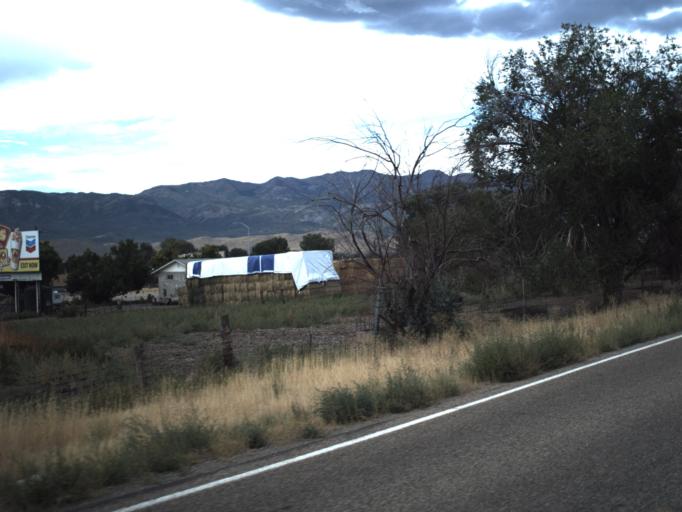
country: US
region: Utah
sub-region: Morgan County
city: Morgan
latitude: 41.0451
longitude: -111.6681
